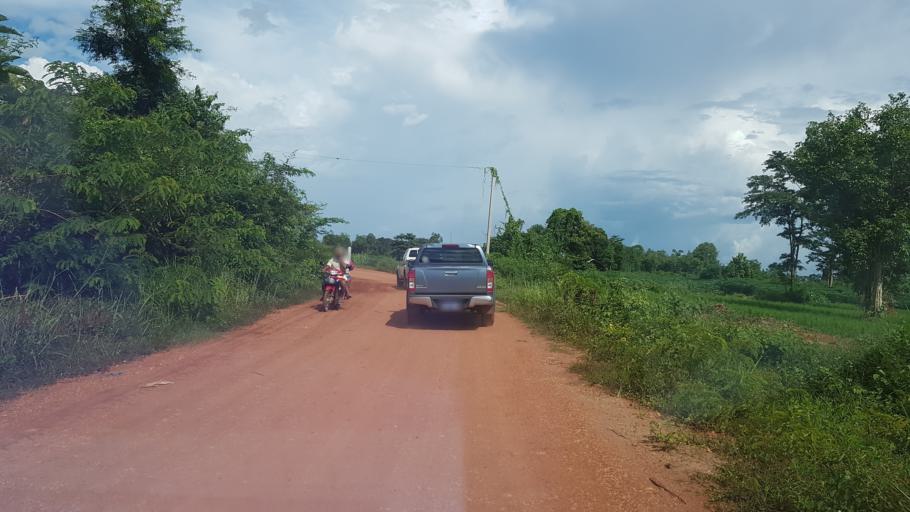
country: LA
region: Vientiane
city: Vientiane
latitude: 18.2052
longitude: 102.5683
